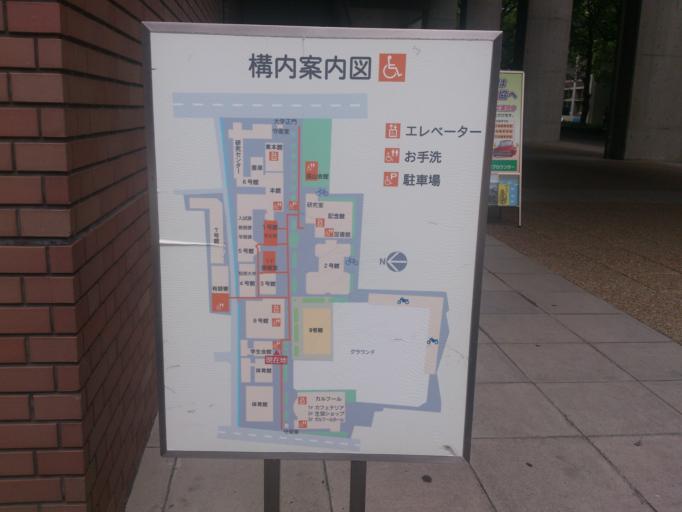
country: JP
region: Ehime
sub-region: Shikoku-chuo Shi
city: Matsuyama
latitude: 33.8510
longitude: 132.7666
